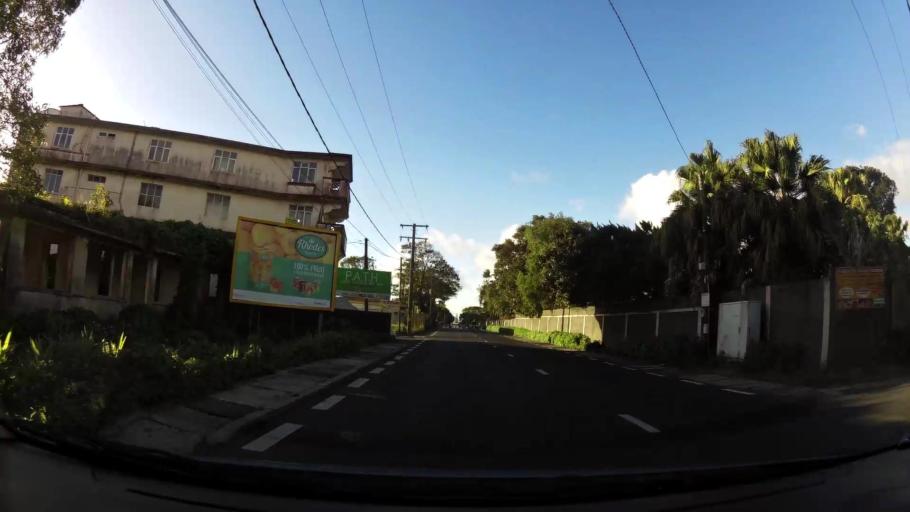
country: MU
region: Plaines Wilhems
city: Curepipe
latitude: -20.3103
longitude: 57.5245
